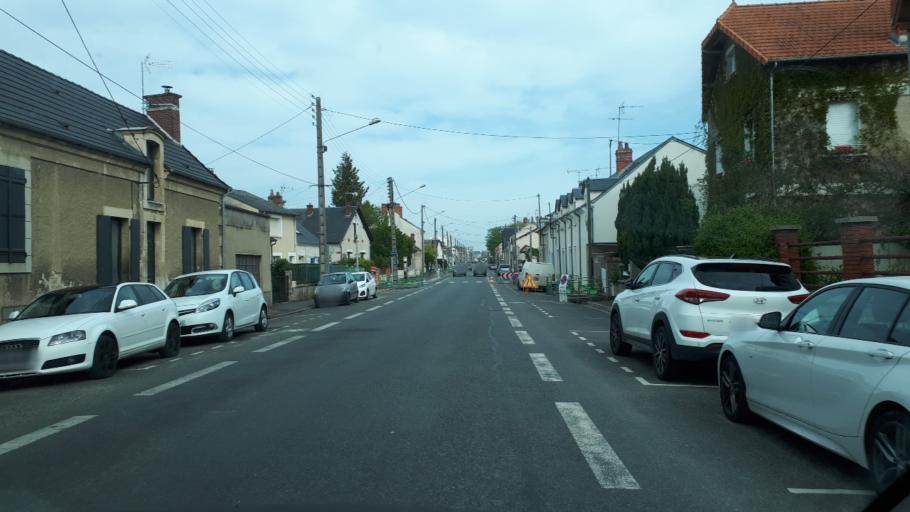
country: FR
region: Centre
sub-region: Departement du Cher
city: Bourges
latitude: 47.0654
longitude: 2.4193
